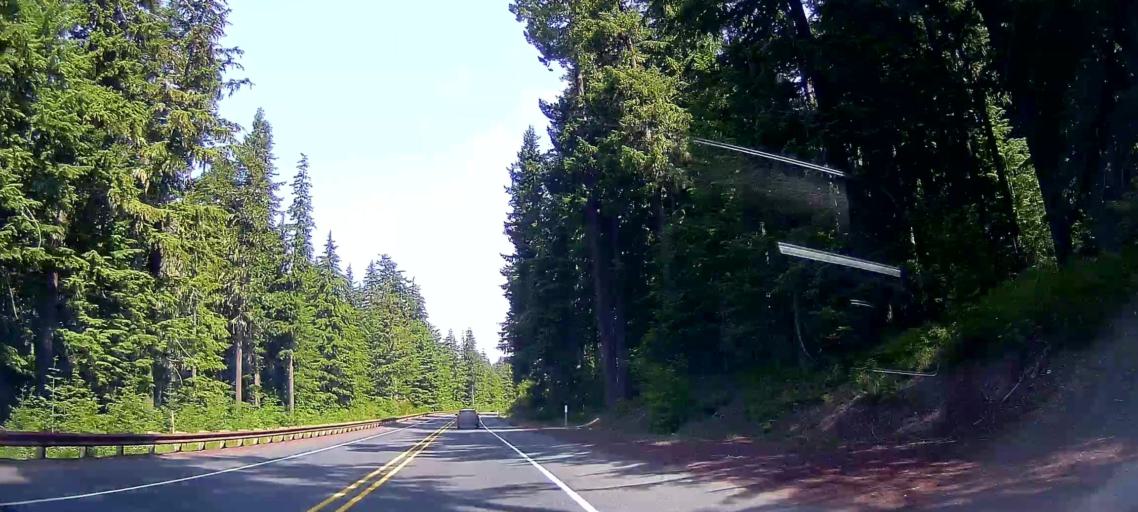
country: US
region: Oregon
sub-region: Clackamas County
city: Mount Hood Village
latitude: 45.2033
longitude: -121.6941
